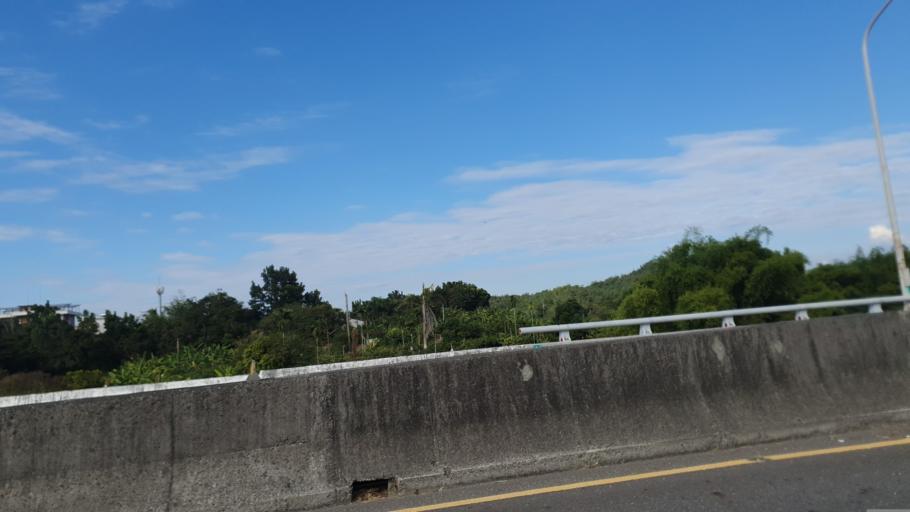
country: TW
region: Taiwan
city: Yujing
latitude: 23.0535
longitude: 120.4118
